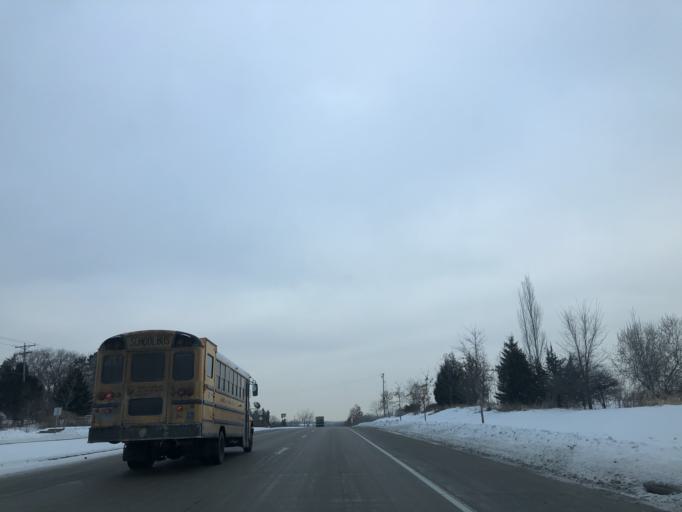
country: US
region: Minnesota
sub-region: Ramsey County
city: Shoreview
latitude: 45.0794
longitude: -93.1619
